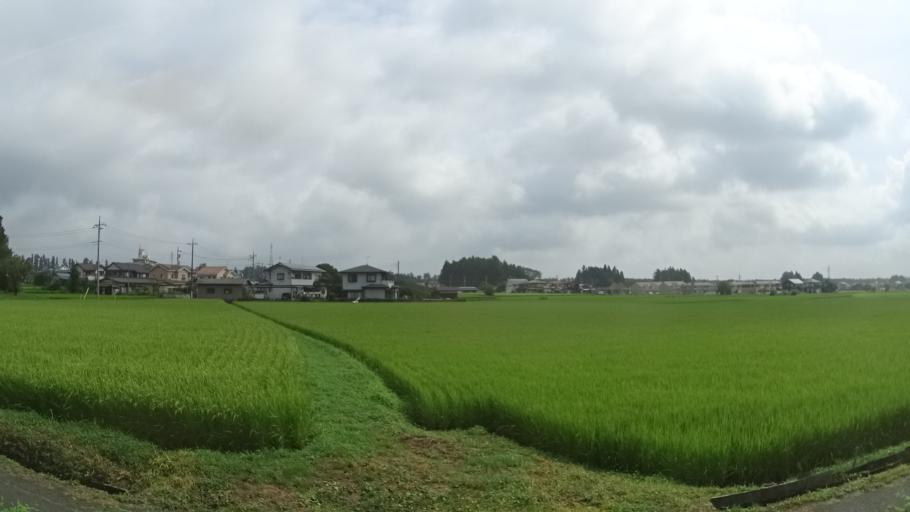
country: JP
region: Tochigi
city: Imaichi
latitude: 36.7131
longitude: 139.6984
